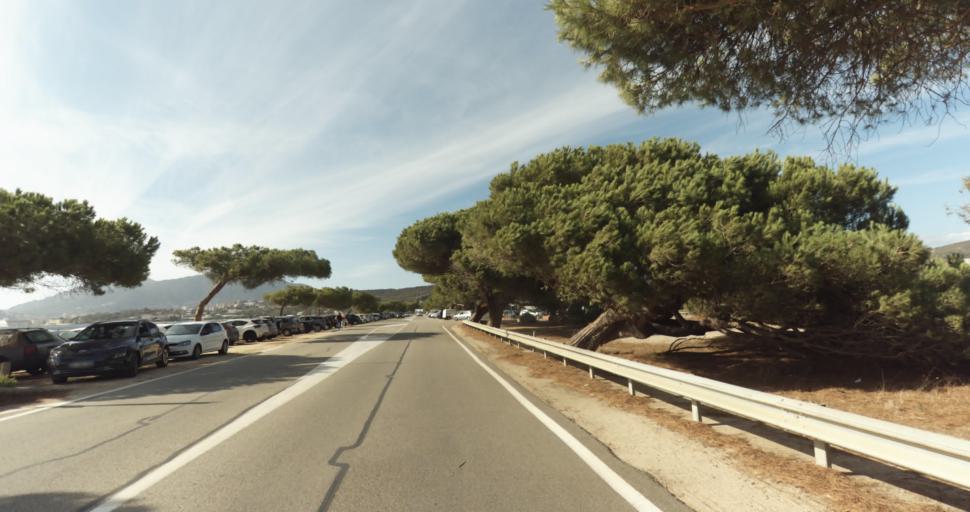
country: FR
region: Corsica
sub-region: Departement de la Corse-du-Sud
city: Ajaccio
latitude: 41.9206
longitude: 8.7879
